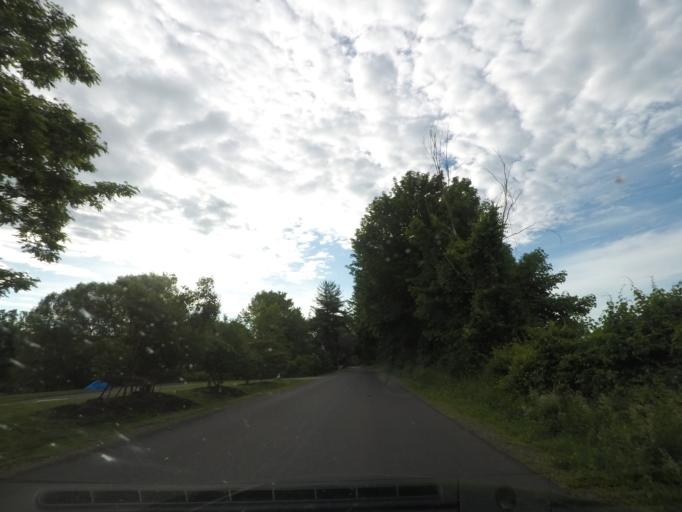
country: US
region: New York
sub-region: Dutchess County
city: Pine Plains
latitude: 41.9589
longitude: -73.4966
